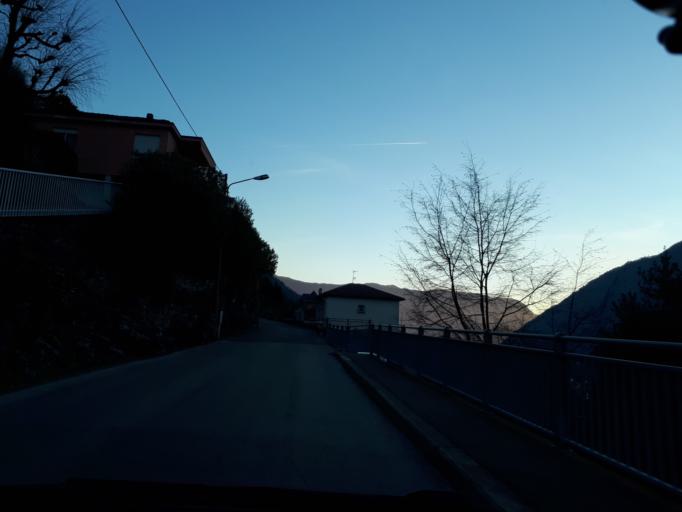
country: IT
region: Lombardy
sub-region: Provincia di Como
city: Nesso
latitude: 45.9170
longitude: 9.1537
